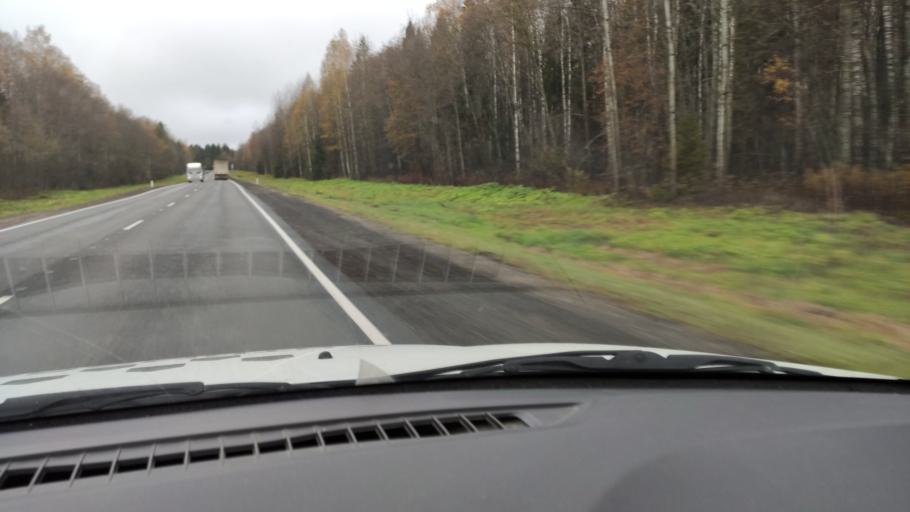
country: RU
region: Kirov
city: Belaya Kholunitsa
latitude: 58.8294
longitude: 50.6415
